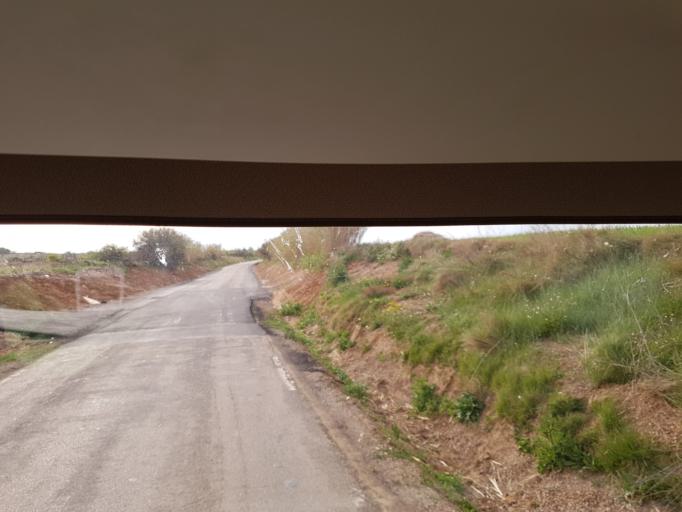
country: FR
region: Languedoc-Roussillon
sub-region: Departement de l'Herault
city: Marseillan
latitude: 43.3650
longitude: 3.5169
